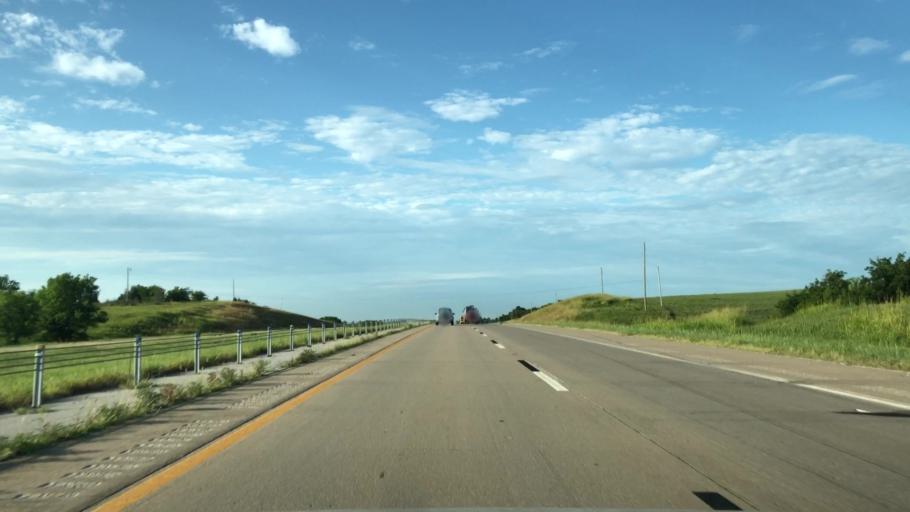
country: US
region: Oklahoma
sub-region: Osage County
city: Skiatook
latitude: 36.4803
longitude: -95.9207
